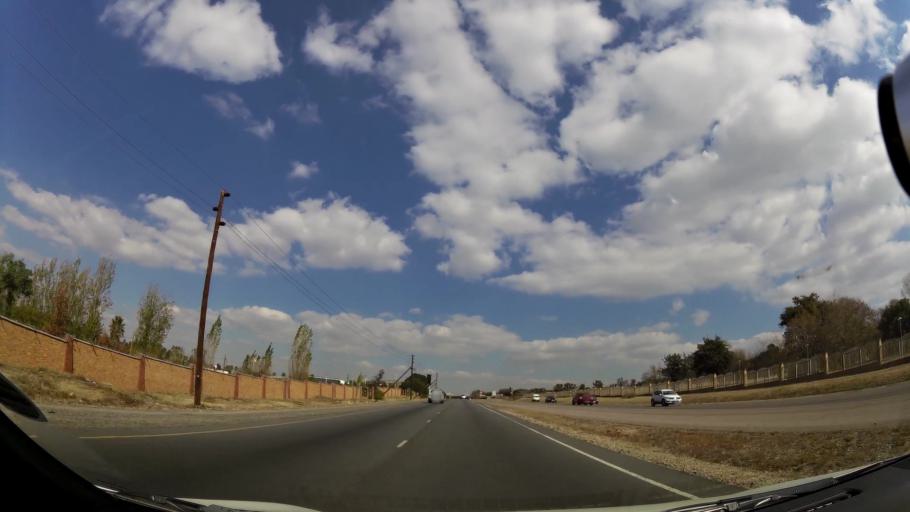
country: ZA
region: Gauteng
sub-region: City of Johannesburg Metropolitan Municipality
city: Midrand
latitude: -26.0390
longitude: 28.0910
